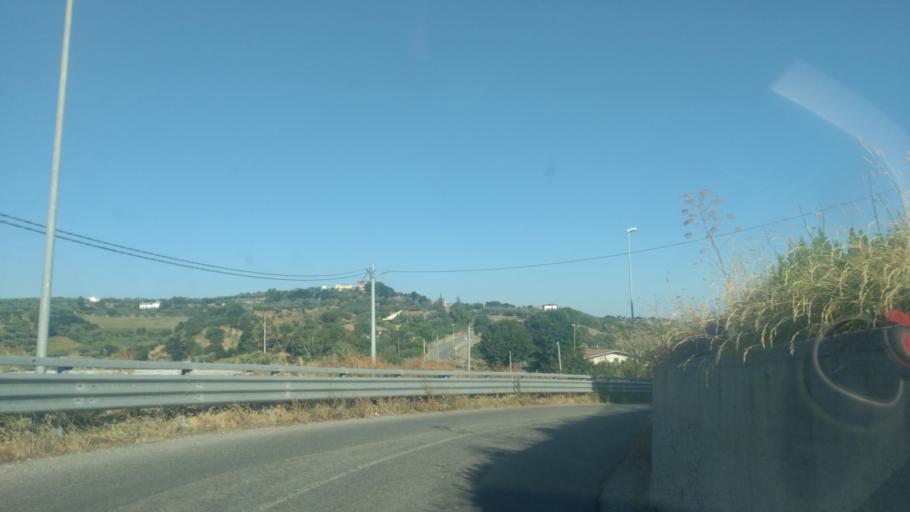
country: IT
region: Calabria
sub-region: Provincia di Catanzaro
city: Staletti
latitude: 38.7659
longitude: 16.5310
